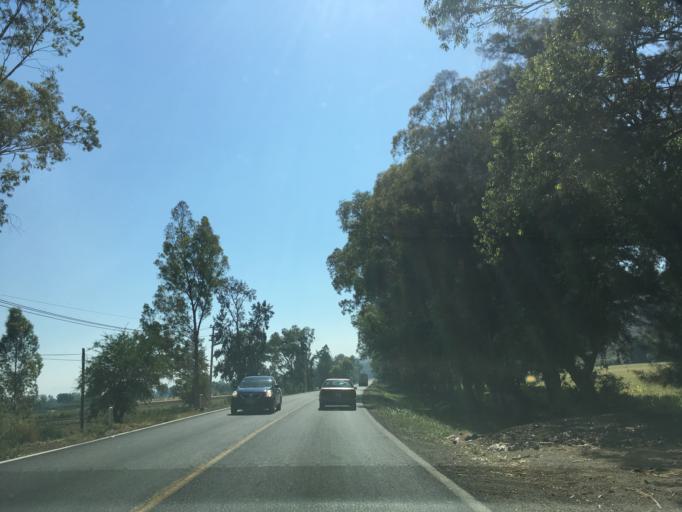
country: MX
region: Michoacan
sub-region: Indaparapeo
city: Colonia de Guadalupe
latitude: 19.8028
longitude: -100.9111
